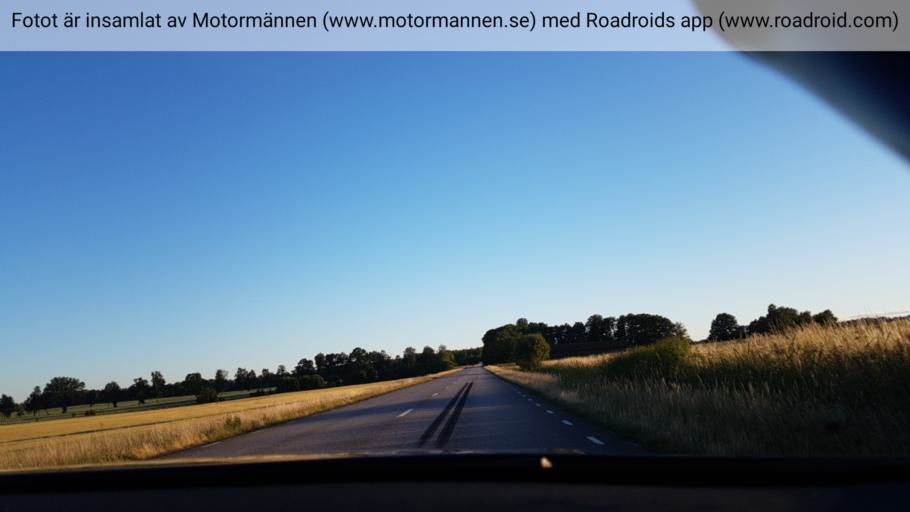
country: SE
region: Vaestra Goetaland
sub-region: Hjo Kommun
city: Hjo
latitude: 58.3272
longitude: 14.3246
